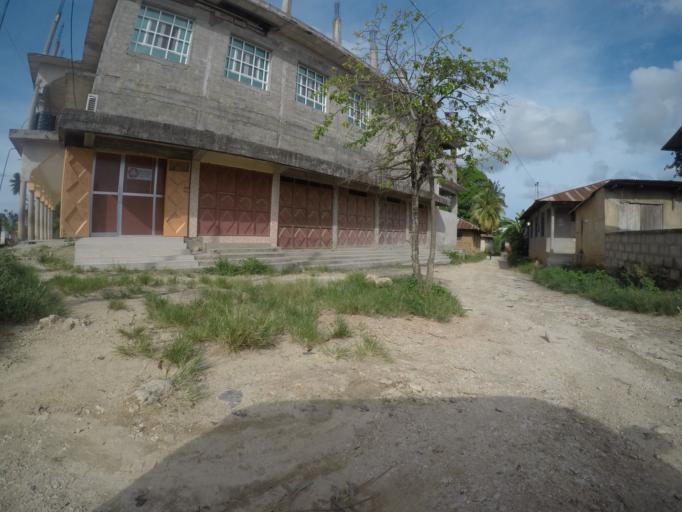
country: TZ
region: Pemba South
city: Chake Chake
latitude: -5.2267
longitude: 39.7755
